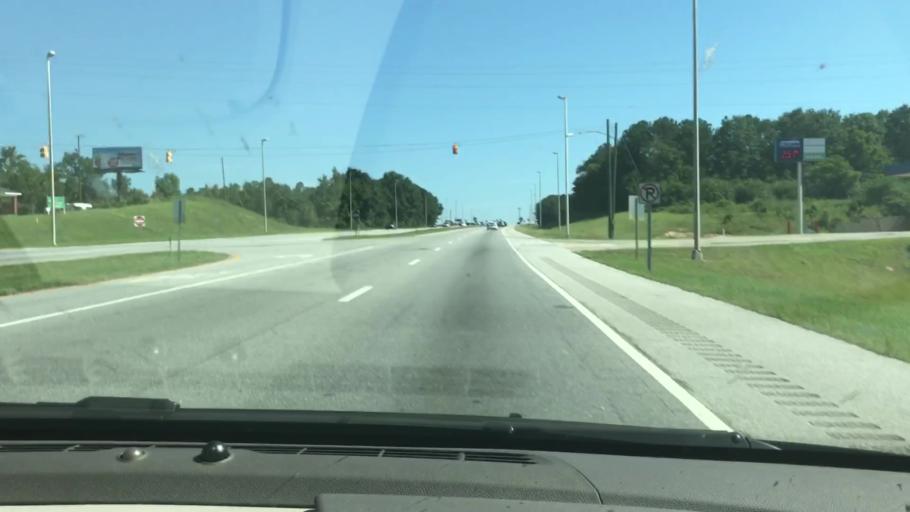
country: US
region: Alabama
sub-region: Russell County
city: Phenix City
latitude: 32.4475
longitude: -85.0172
